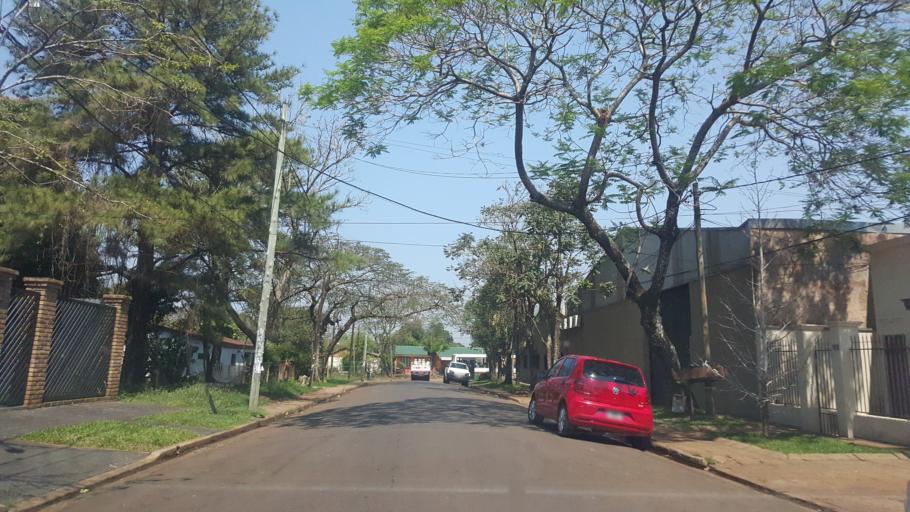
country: AR
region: Misiones
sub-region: Departamento de Capital
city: Posadas
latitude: -27.3716
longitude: -55.9158
